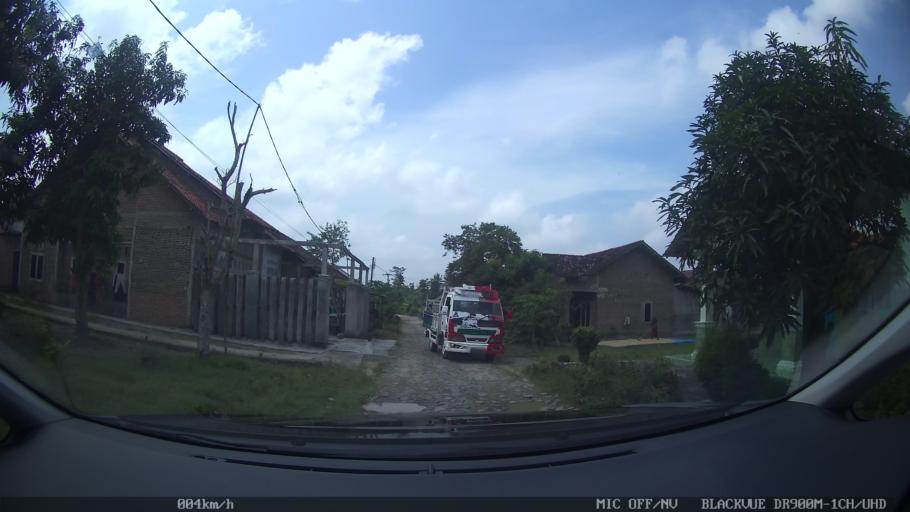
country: ID
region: Lampung
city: Kedaton
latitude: -5.3321
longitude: 105.3011
